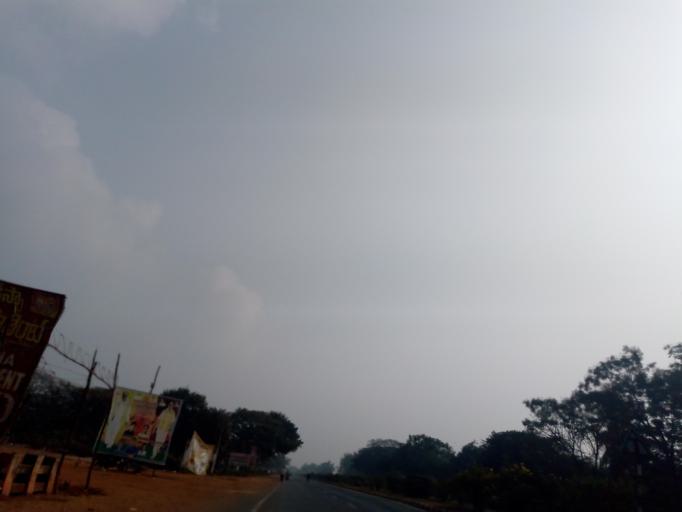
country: IN
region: Andhra Pradesh
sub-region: West Godavari
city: Tadepallegudem
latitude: 16.8110
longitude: 81.3680
